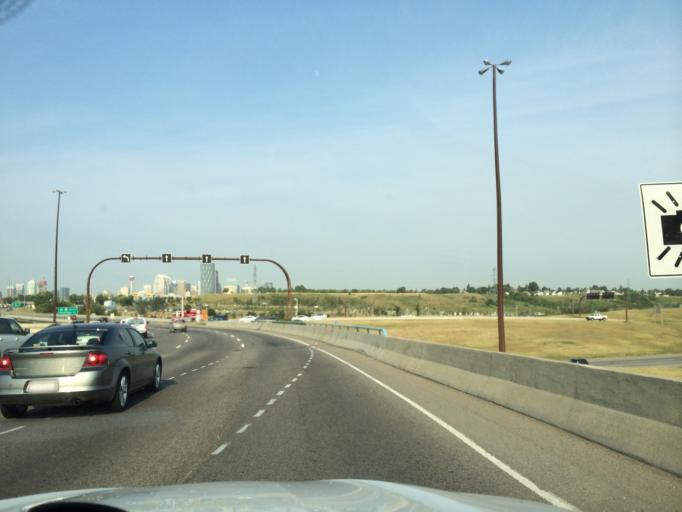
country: CA
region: Alberta
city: Calgary
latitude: 51.0492
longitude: -114.0169
